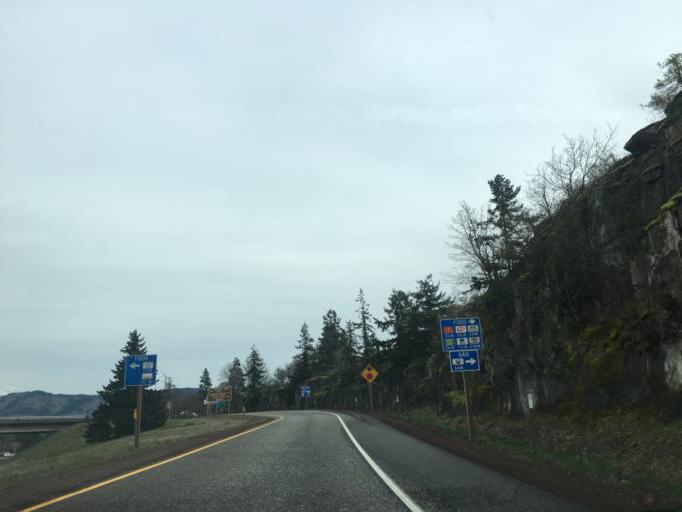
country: US
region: Oregon
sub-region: Hood River County
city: Hood River
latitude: 45.7107
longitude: -121.5518
